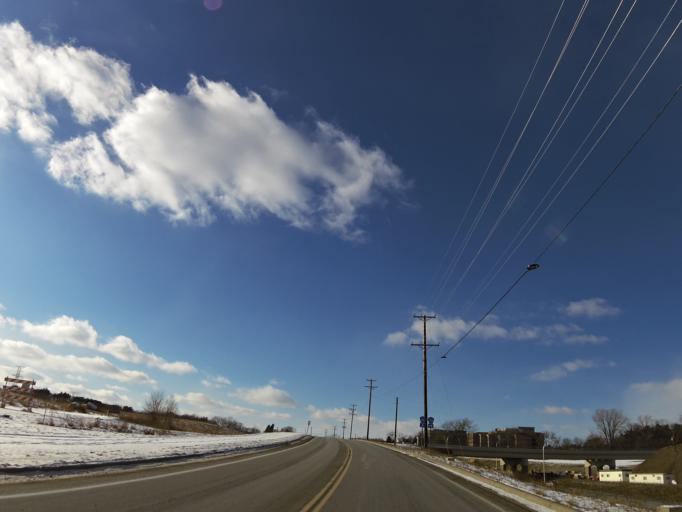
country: US
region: Minnesota
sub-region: Washington County
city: Oak Park Heights
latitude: 45.0349
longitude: -92.7956
